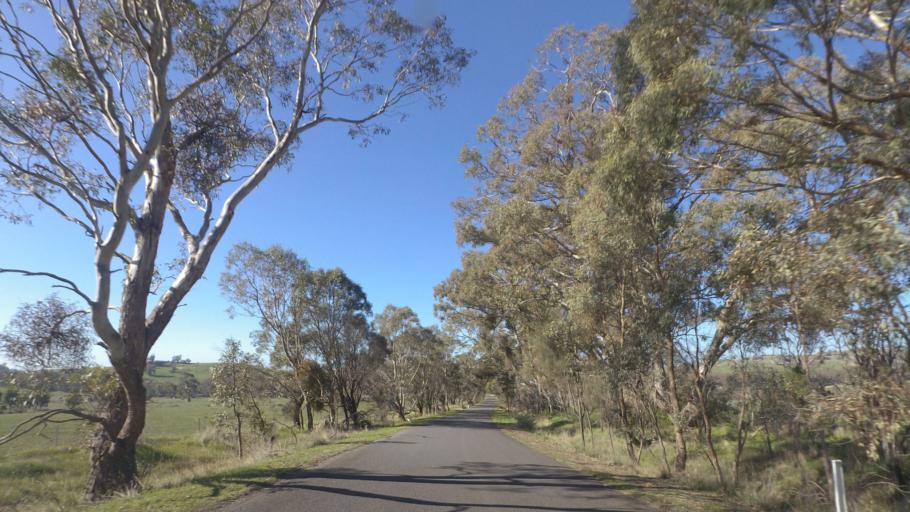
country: AU
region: Victoria
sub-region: Mount Alexander
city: Castlemaine
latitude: -36.9683
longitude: 144.3108
